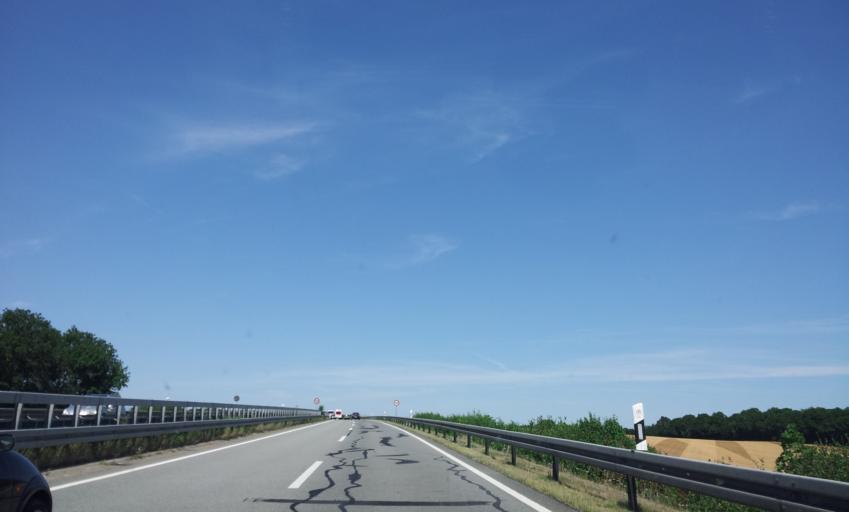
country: DE
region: Mecklenburg-Vorpommern
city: Brandshagen
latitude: 54.2230
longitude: 13.1541
